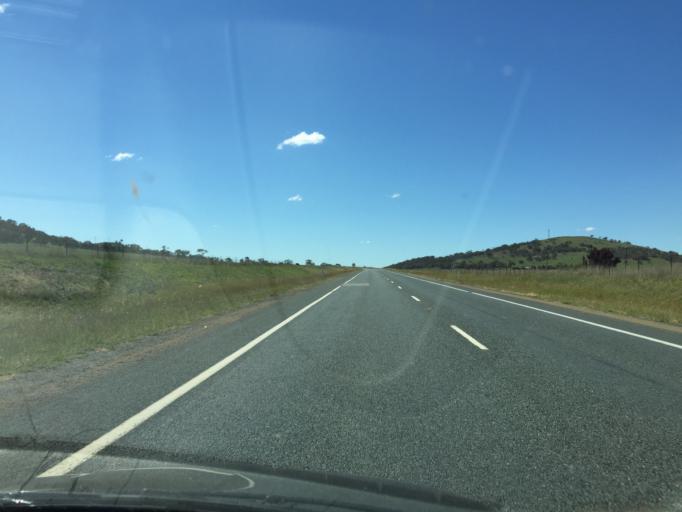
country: AU
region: Australian Capital Territory
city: Macarthur
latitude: -35.4848
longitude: 149.1483
